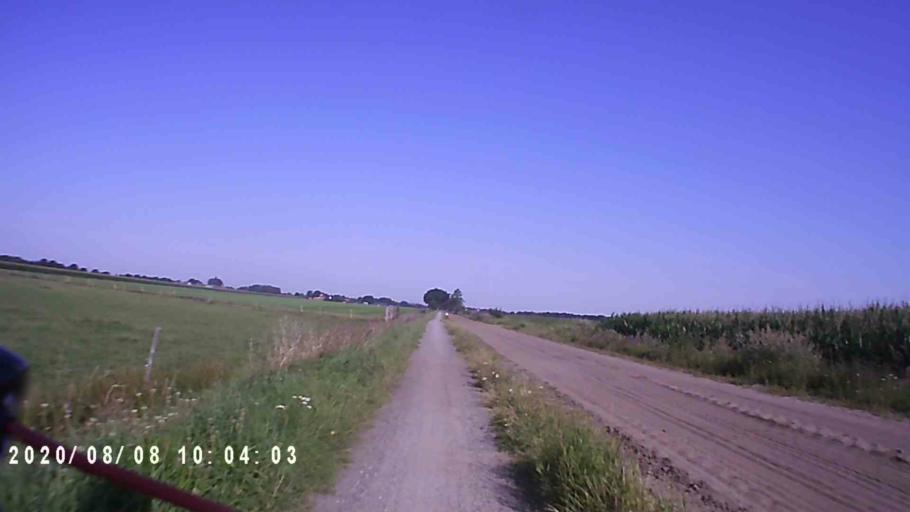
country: NL
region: Groningen
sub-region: Gemeente Leek
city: Leek
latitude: 53.1102
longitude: 6.3785
